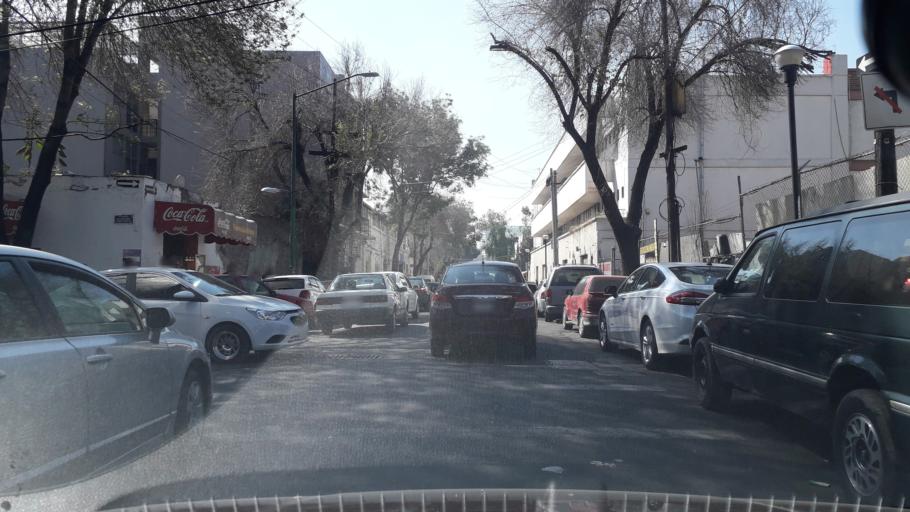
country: MX
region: Mexico City
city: Cuauhtemoc
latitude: 19.4434
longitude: -99.1509
